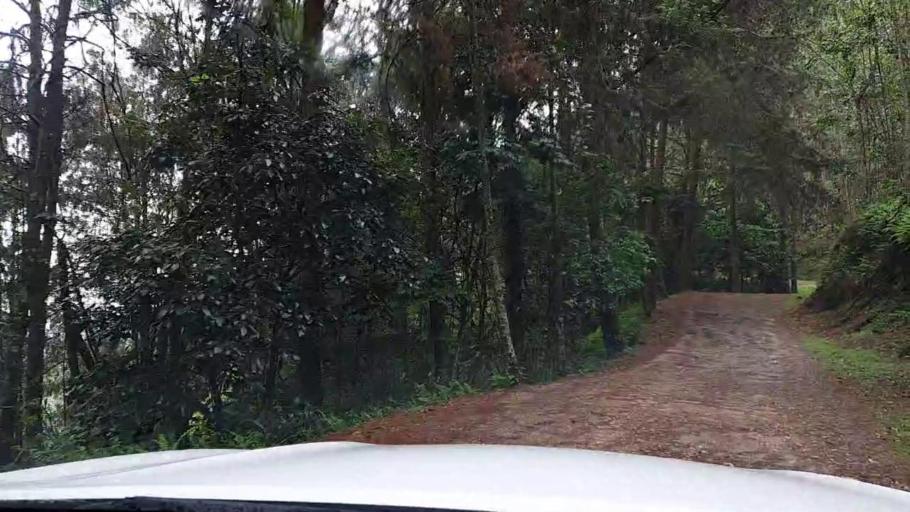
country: RW
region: Western Province
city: Cyangugu
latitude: -2.5588
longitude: 28.9889
